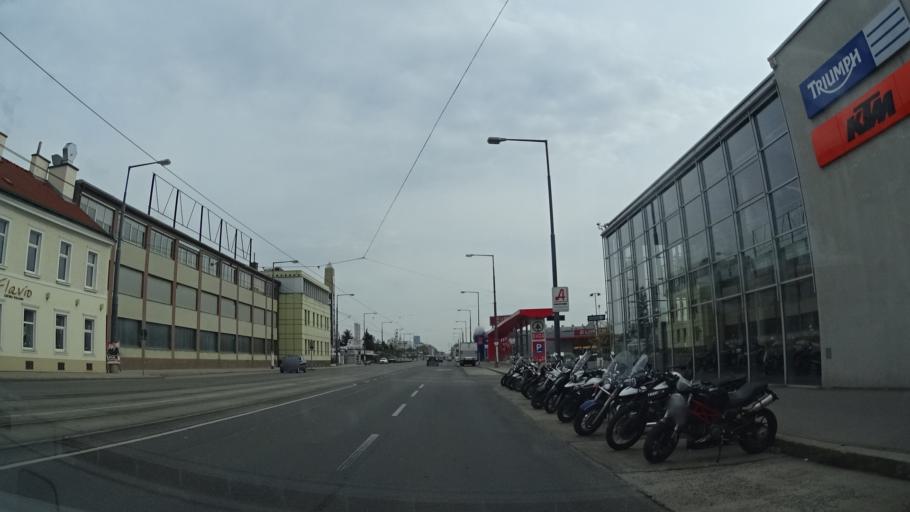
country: AT
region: Lower Austria
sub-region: Politischer Bezirk Korneuburg
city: Langenzersdorf
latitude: 48.2763
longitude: 16.3885
